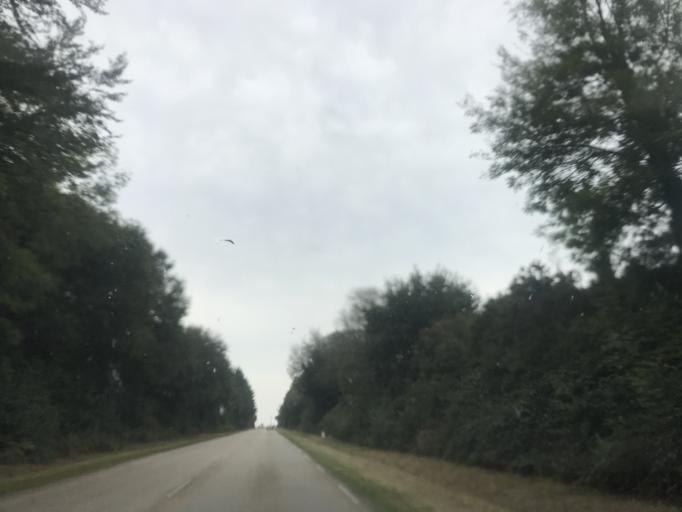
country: FR
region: Brittany
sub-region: Departement du Finistere
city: Plouneour-Menez
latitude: 48.4600
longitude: -3.8767
